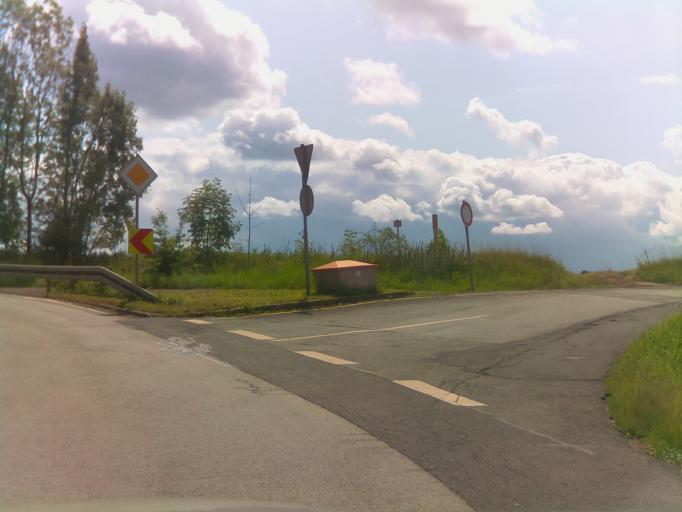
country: DE
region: Bavaria
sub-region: Upper Franconia
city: Rodental
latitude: 50.2908
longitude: 11.0895
